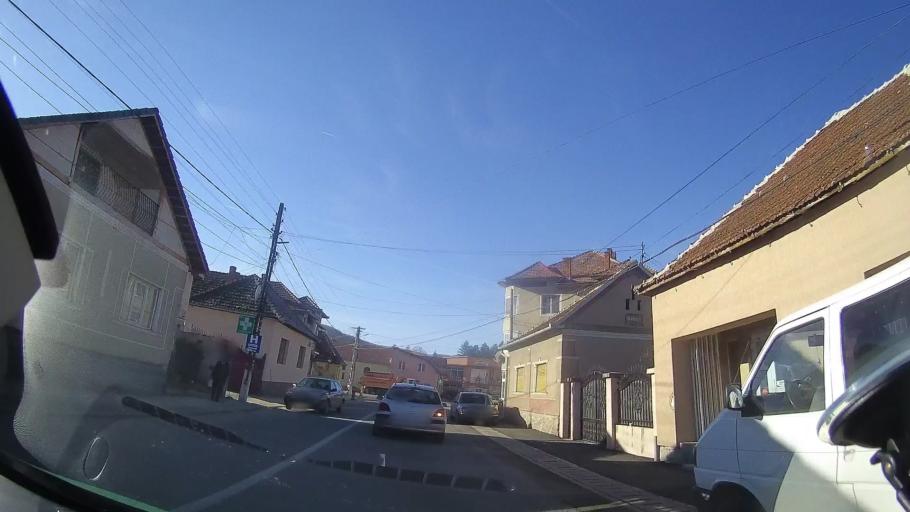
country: RO
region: Bihor
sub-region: Comuna Bratca
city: Bratca
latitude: 46.9271
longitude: 22.6034
